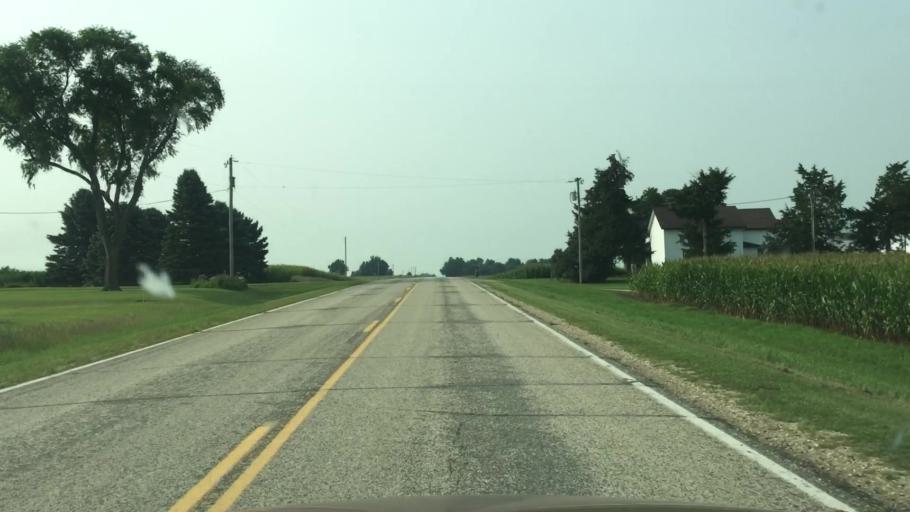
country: US
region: Iowa
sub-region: O'Brien County
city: Sheldon
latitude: 43.2704
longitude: -95.7829
